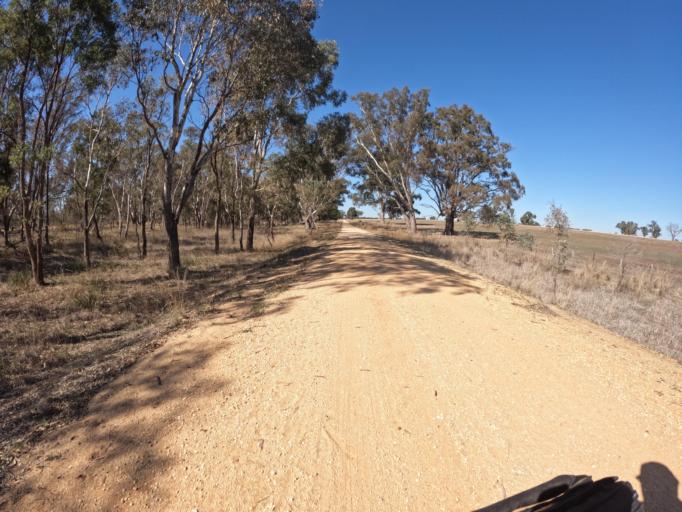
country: AU
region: Victoria
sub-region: Greater Bendigo
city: Kennington
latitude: -36.8335
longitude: 144.5946
